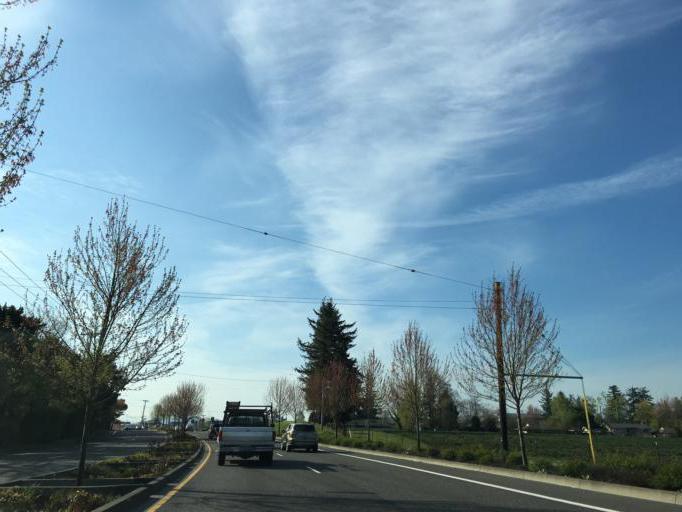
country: US
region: Oregon
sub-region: Multnomah County
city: Wood Village
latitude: 45.5221
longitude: -122.4132
